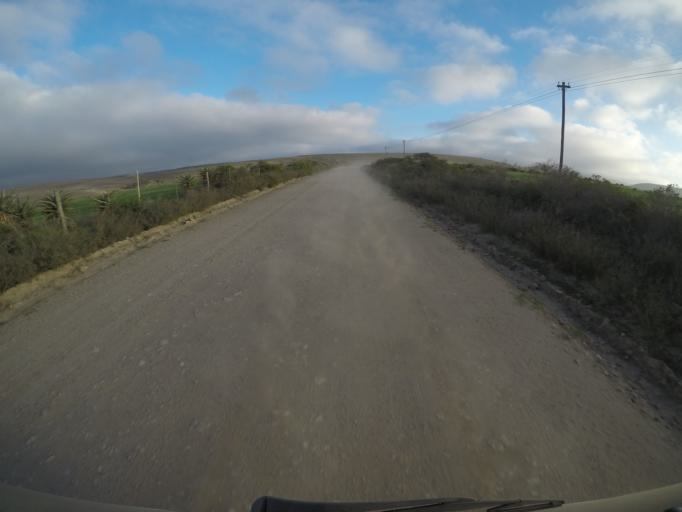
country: ZA
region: Western Cape
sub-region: Eden District Municipality
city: Mossel Bay
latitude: -34.1215
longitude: 22.0534
